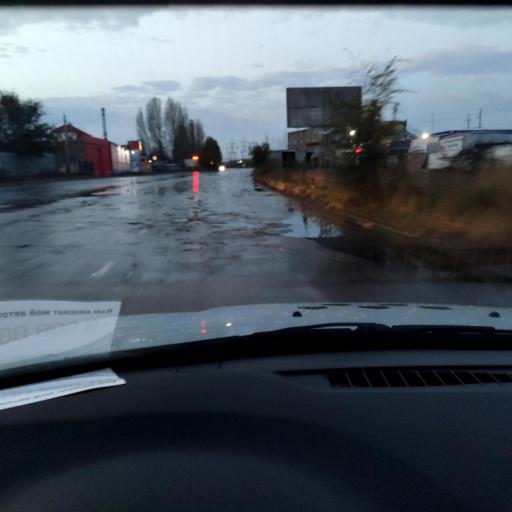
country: RU
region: Samara
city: Tol'yatti
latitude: 53.5221
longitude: 49.4694
